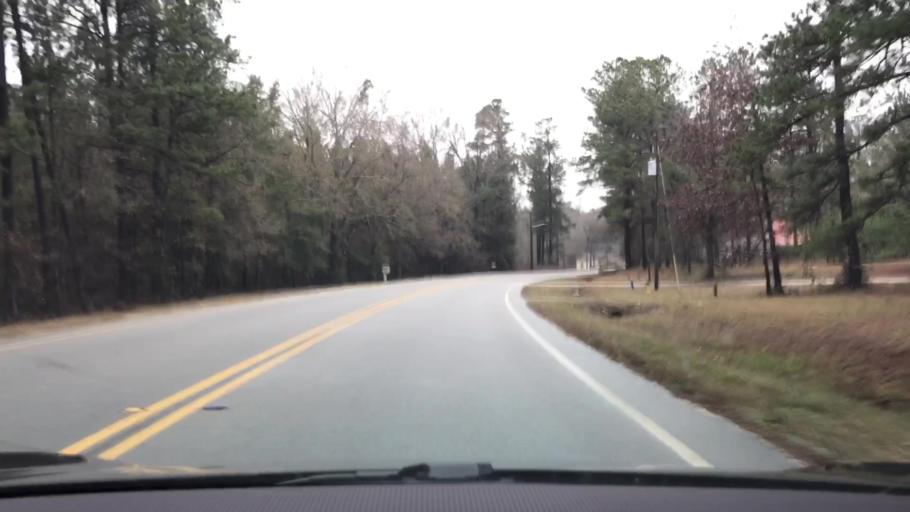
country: US
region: Georgia
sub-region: Jefferson County
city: Wrens
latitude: 33.2046
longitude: -82.4686
